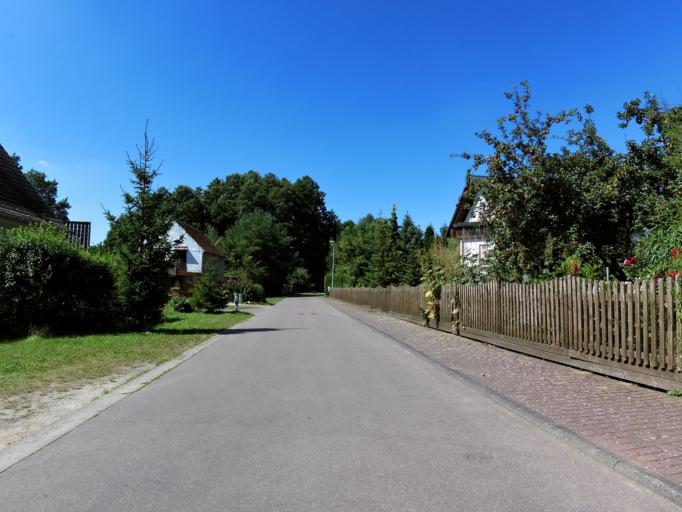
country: DE
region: Saxony
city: Torgau
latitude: 51.5123
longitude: 13.0274
